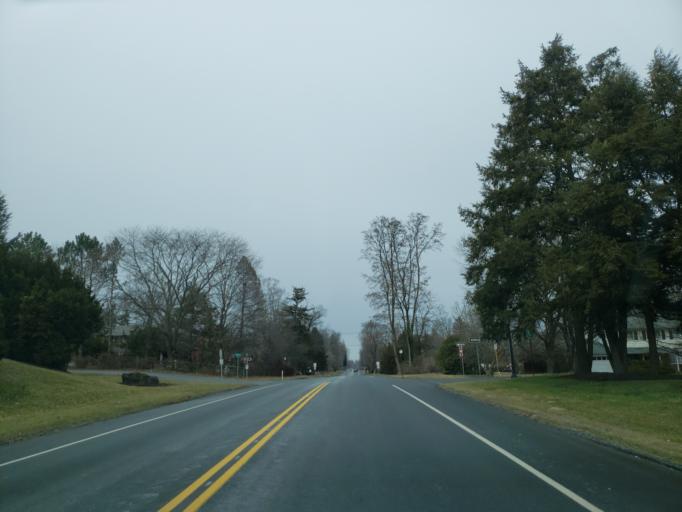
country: US
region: Pennsylvania
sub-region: Lehigh County
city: Dorneyville
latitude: 40.6023
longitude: -75.5293
